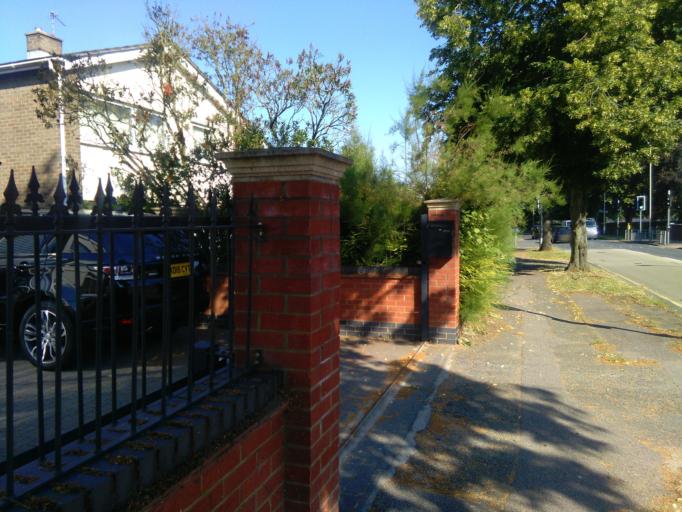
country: GB
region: England
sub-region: Bedford
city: Bedford
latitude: 52.1505
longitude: -0.4581
